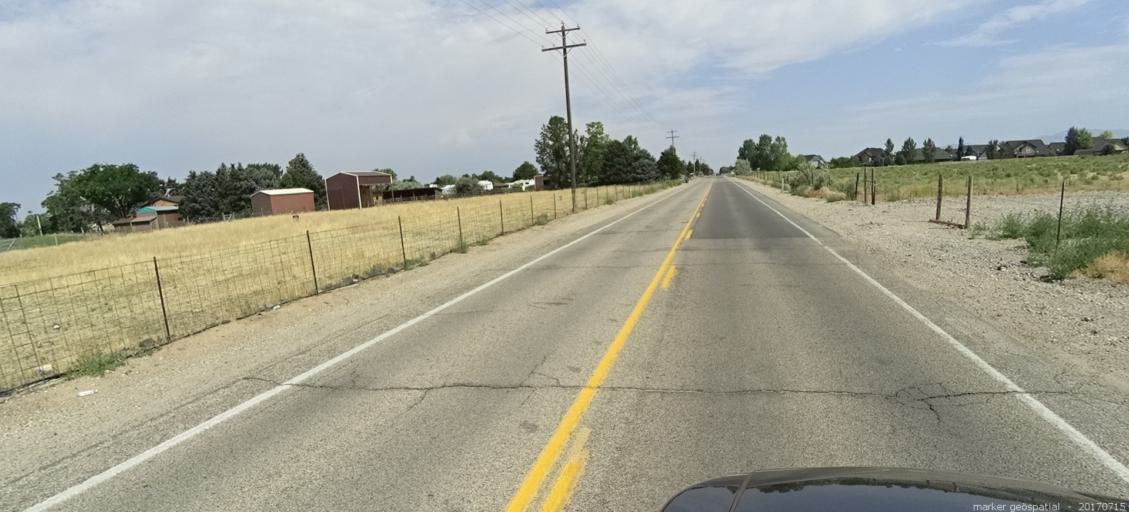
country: US
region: Idaho
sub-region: Ada County
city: Garden City
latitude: 43.5444
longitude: -116.2742
